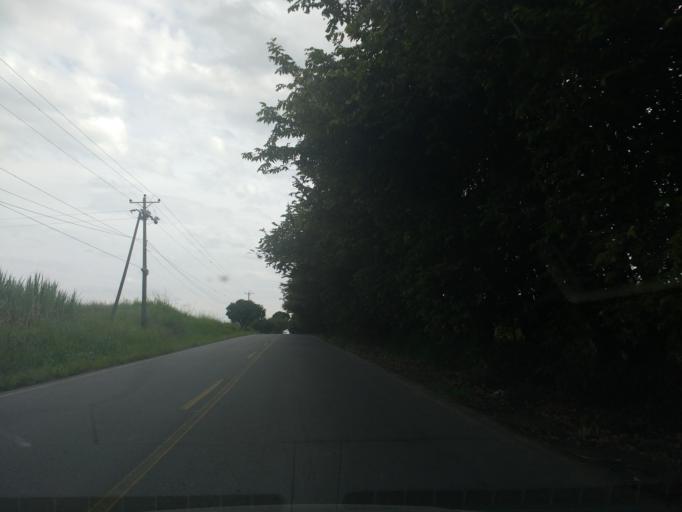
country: CO
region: Valle del Cauca
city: Florida
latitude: 3.2906
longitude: -76.2271
